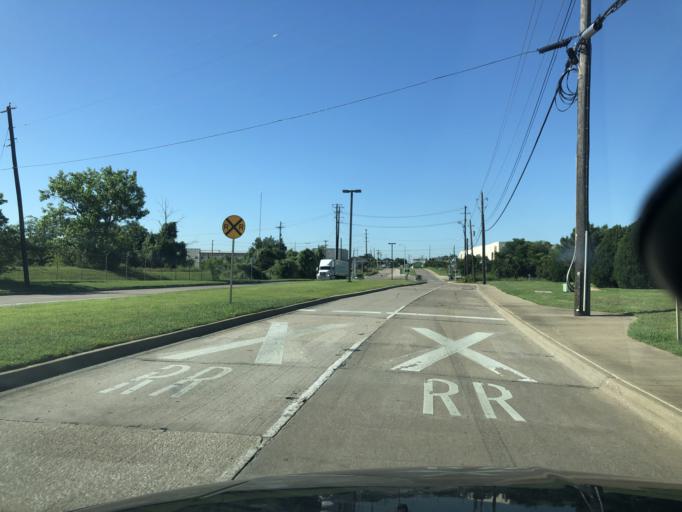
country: US
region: Texas
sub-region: Tarrant County
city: Euless
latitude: 32.8181
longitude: -97.0305
